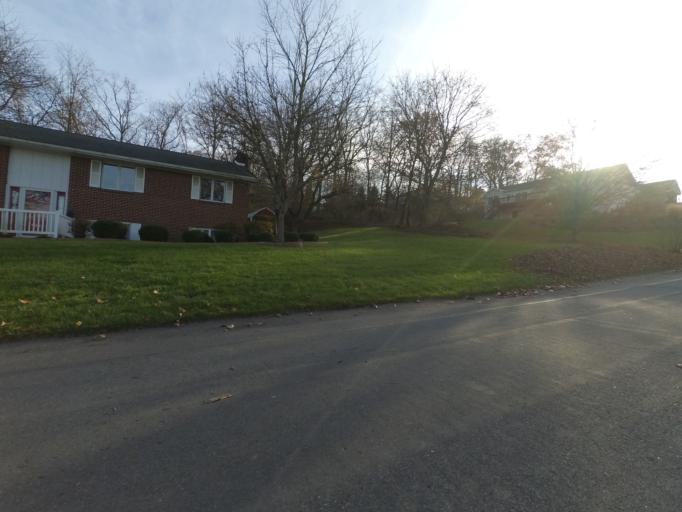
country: US
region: Pennsylvania
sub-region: Centre County
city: Lemont
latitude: 40.8045
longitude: -77.8204
